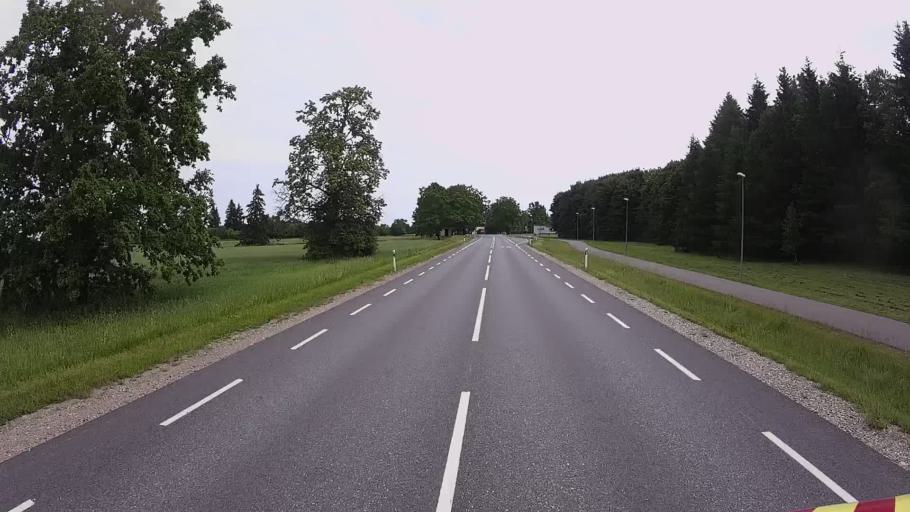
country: EE
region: Viljandimaa
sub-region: Karksi vald
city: Karksi-Nuia
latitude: 58.1176
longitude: 25.5784
